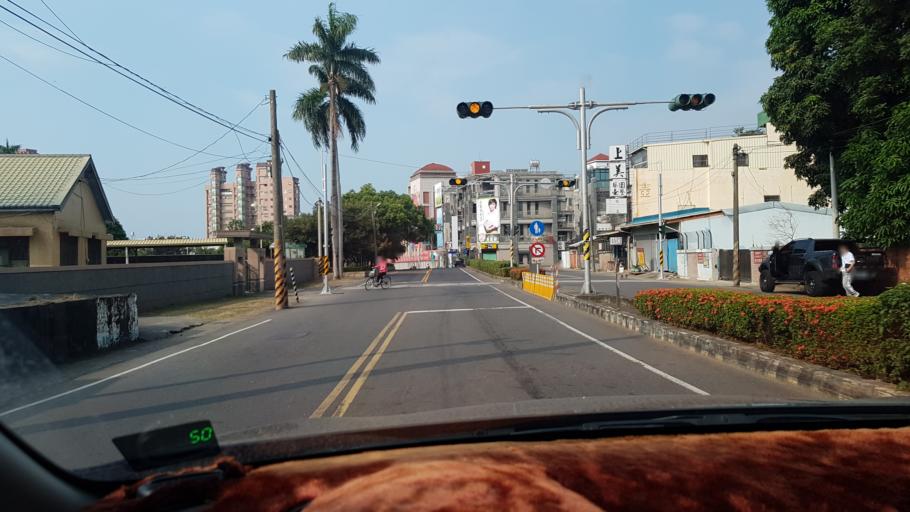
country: TW
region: Taiwan
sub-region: Chiayi
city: Jiayi Shi
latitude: 23.4875
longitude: 120.4639
